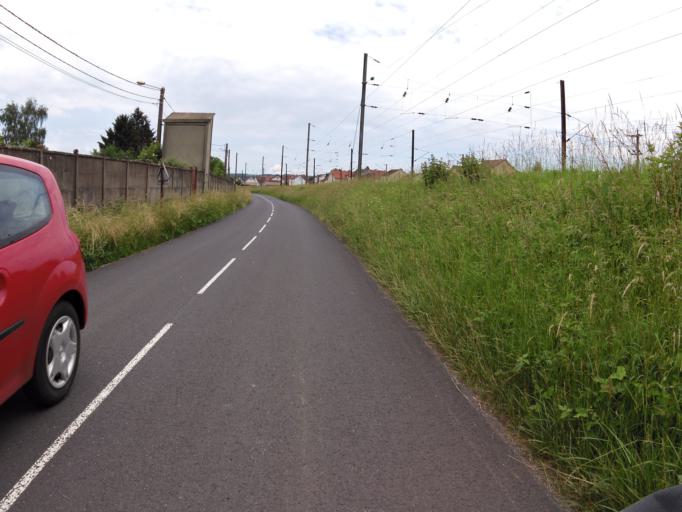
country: FR
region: Champagne-Ardenne
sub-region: Departement des Ardennes
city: Lumes
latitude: 49.7285
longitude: 4.7851
